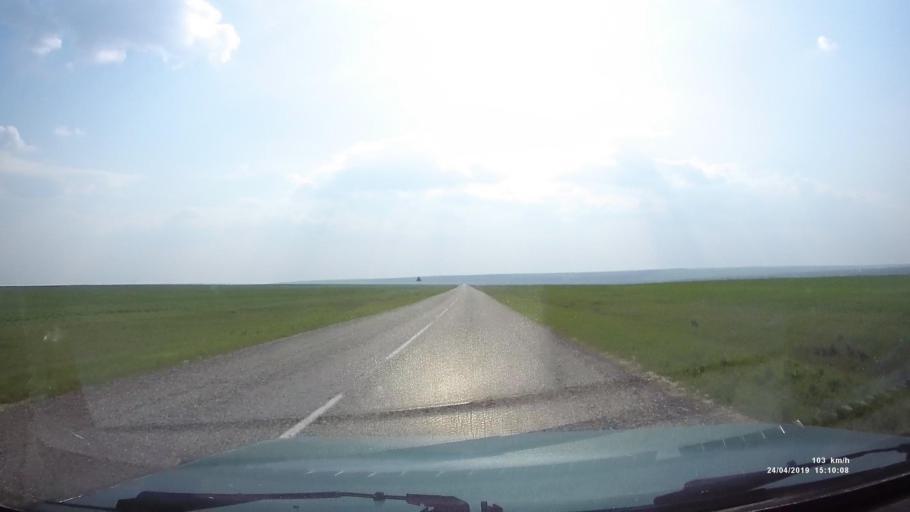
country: RU
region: Rostov
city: Remontnoye
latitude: 46.5522
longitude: 43.3471
